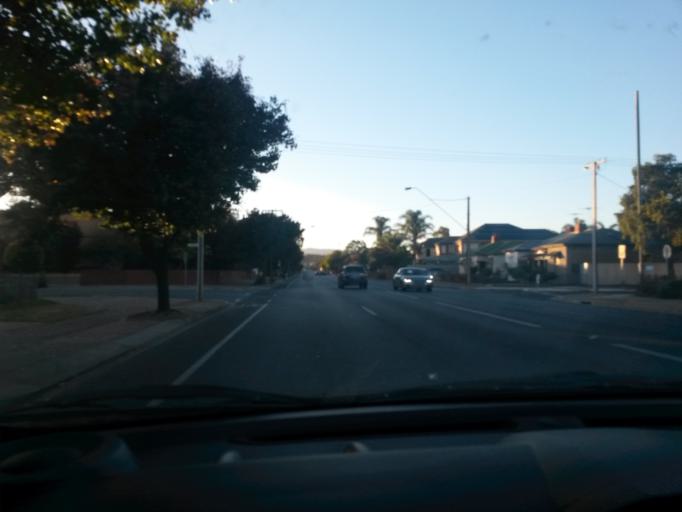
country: AU
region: South Australia
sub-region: Prospect
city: Prospect
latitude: -34.8909
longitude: 138.5744
